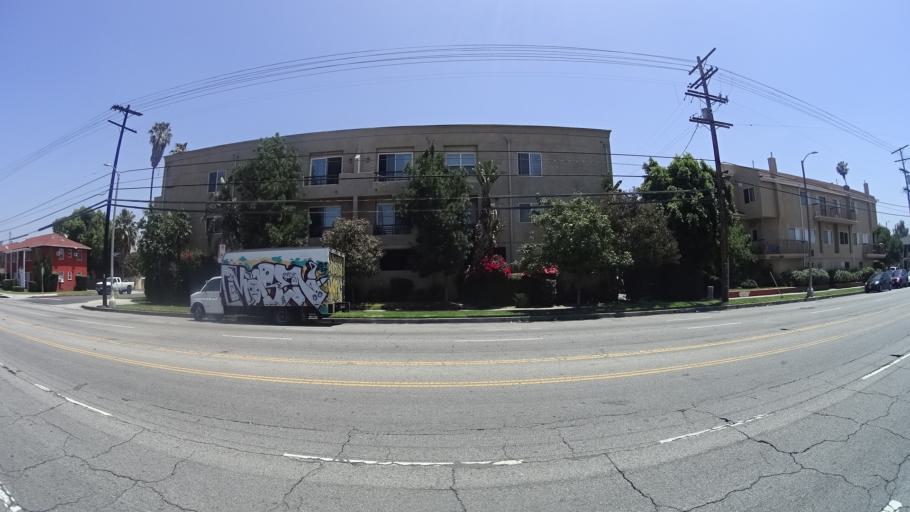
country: US
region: California
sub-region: Los Angeles County
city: Van Nuys
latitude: 34.2037
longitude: -118.4314
